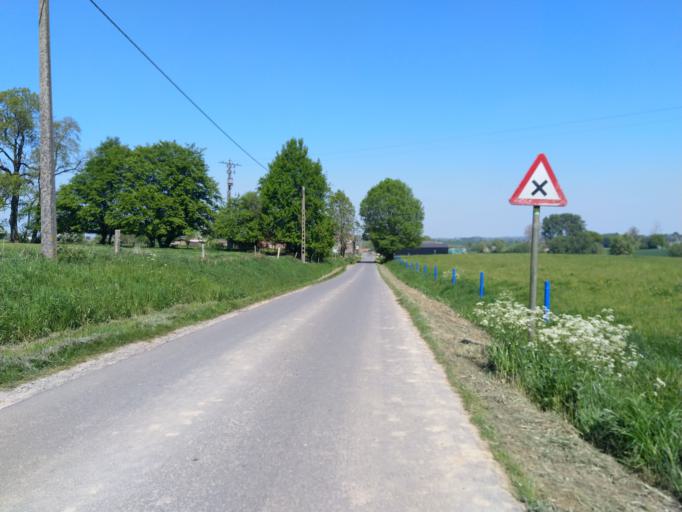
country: BE
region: Wallonia
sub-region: Province du Hainaut
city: Enghien
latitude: 50.6380
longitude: 4.0229
